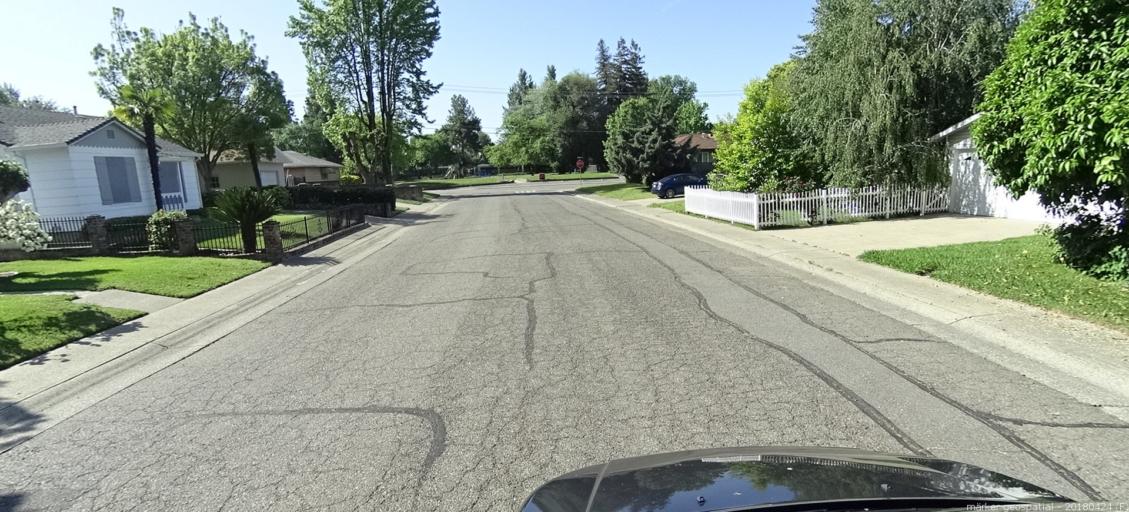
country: US
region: California
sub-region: Yolo County
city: West Sacramento
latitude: 38.5637
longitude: -121.5306
